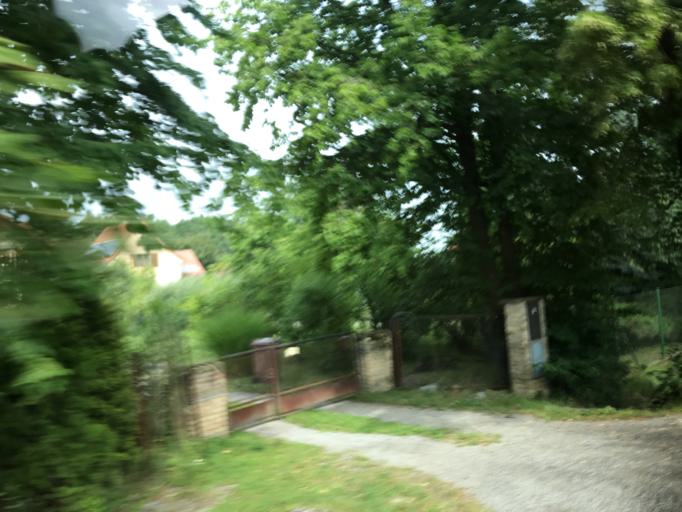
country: CZ
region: Jihocesky
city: Vcelna
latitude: 48.9155
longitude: 14.4512
